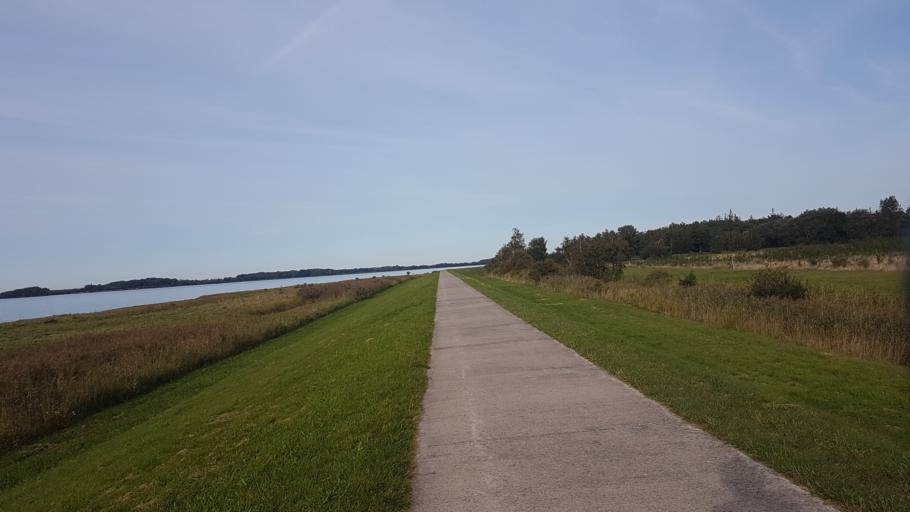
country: DE
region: Mecklenburg-Vorpommern
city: Hiddensee
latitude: 54.4859
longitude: 13.1571
